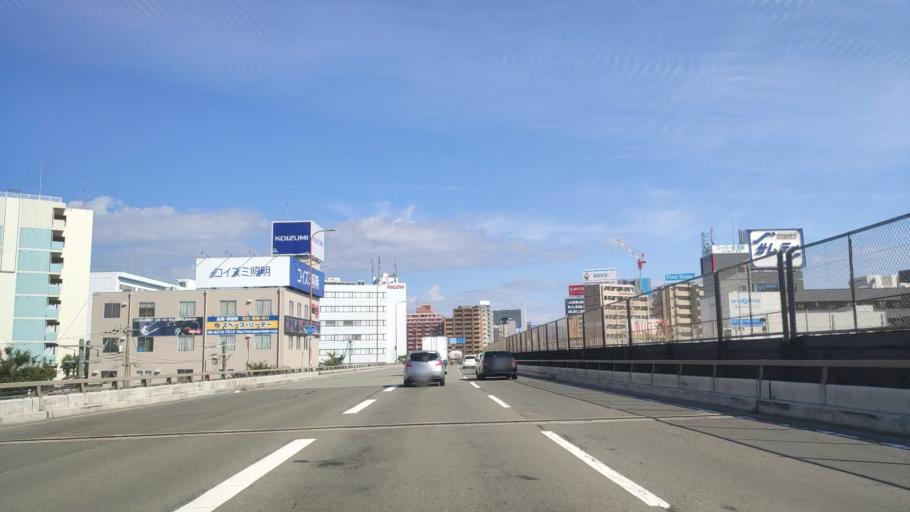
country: JP
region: Osaka
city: Suita
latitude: 34.7507
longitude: 135.4968
